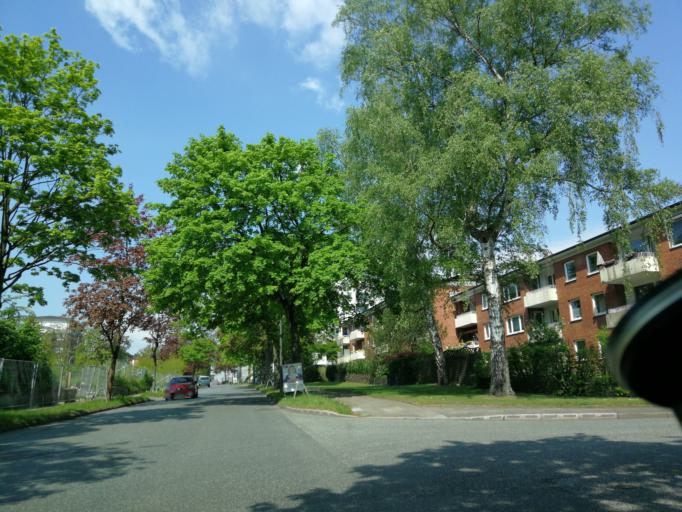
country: DE
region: Schleswig-Holstein
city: Glinde
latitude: 53.5092
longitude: 10.1987
